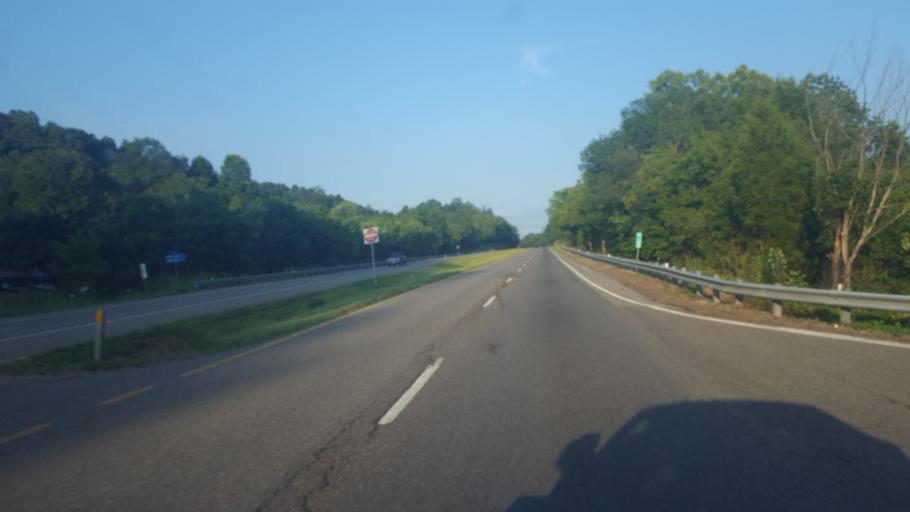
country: US
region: Tennessee
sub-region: Hawkins County
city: Mount Carmel
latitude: 36.6414
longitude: -82.7184
